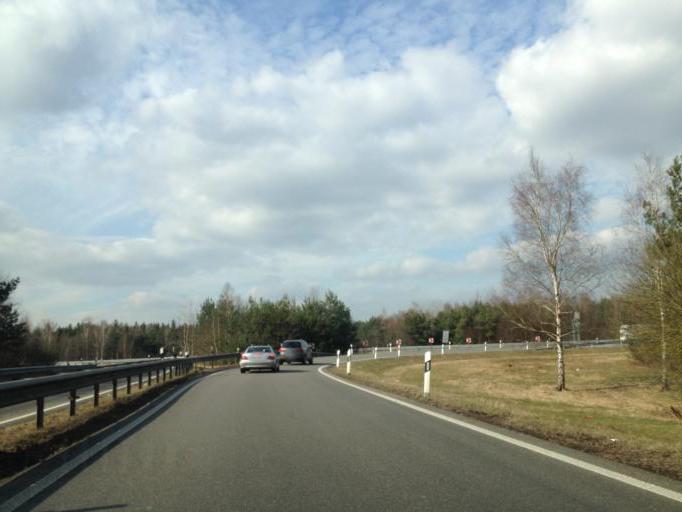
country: DE
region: Rheinland-Pfalz
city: Steinwenden
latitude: 49.4153
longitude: 7.5277
